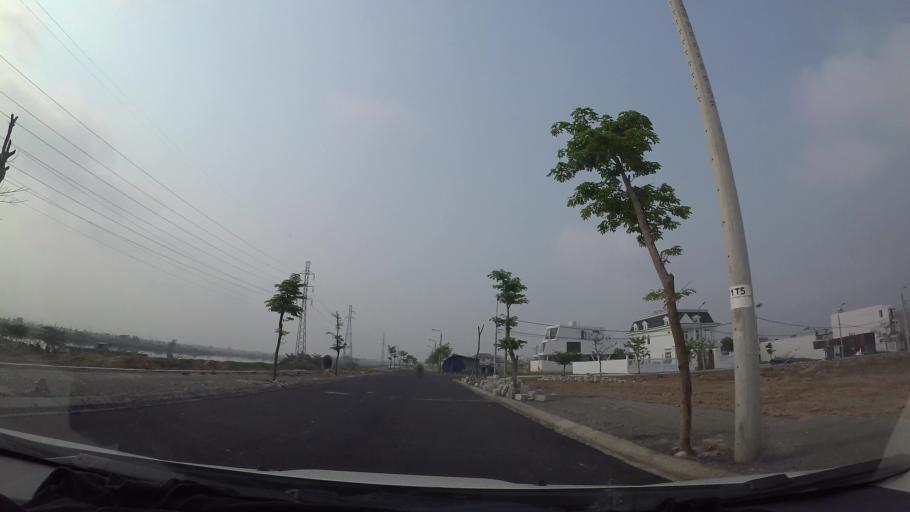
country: VN
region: Da Nang
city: Ngu Hanh Son
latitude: 16.0128
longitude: 108.2318
